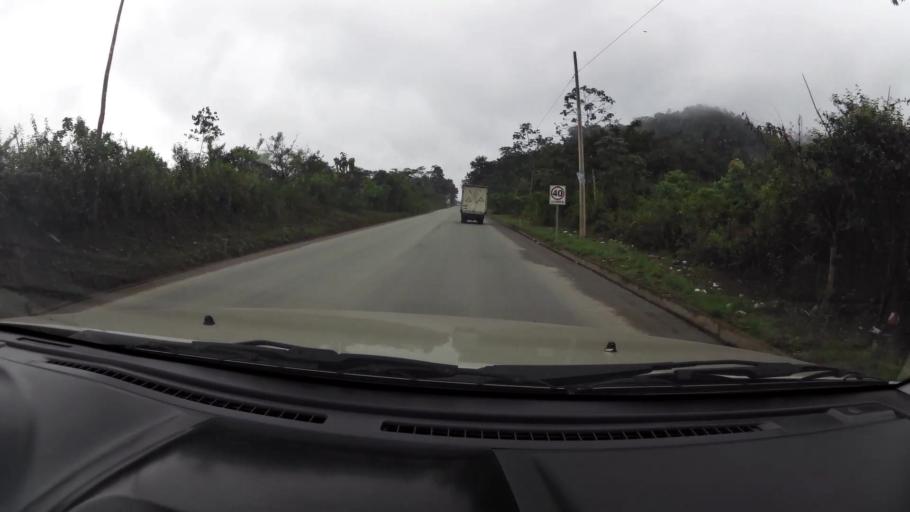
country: EC
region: El Oro
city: Pasaje
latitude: -3.3290
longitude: -79.7644
